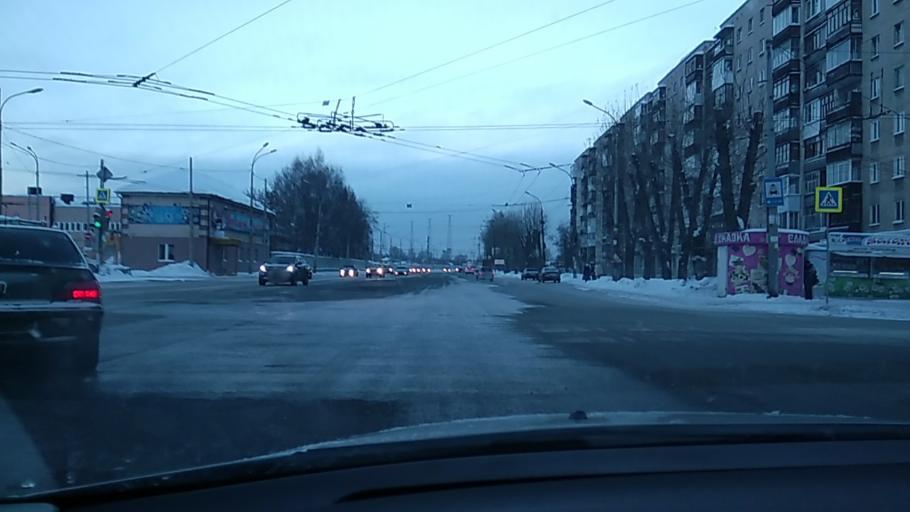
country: RU
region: Sverdlovsk
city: Yekaterinburg
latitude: 56.9093
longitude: 60.5929
